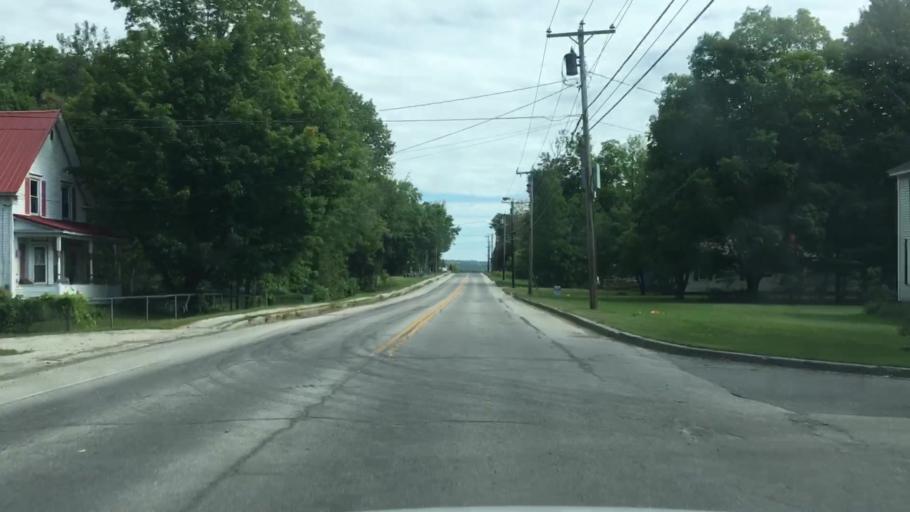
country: US
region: Maine
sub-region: Piscataquis County
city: Dover-Foxcroft
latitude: 45.1917
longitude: -69.2217
